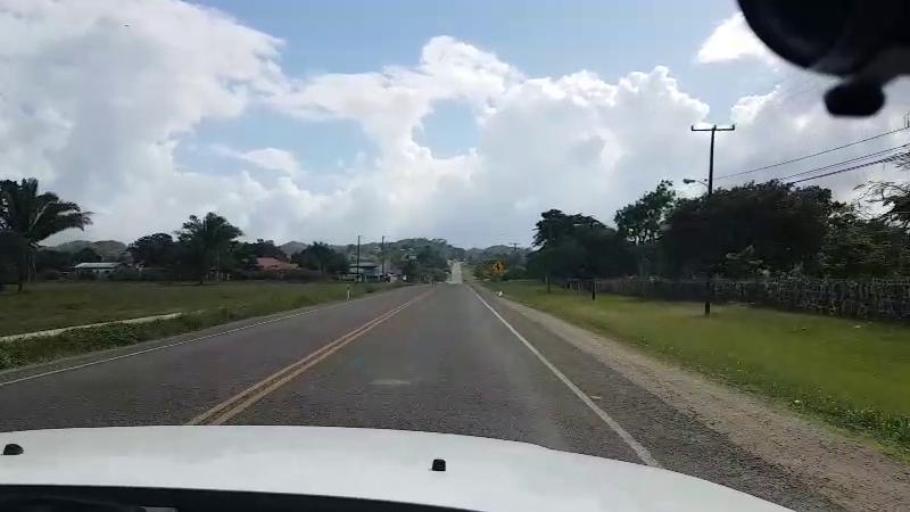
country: BZ
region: Cayo
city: Belmopan
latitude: 17.2393
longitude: -88.7816
